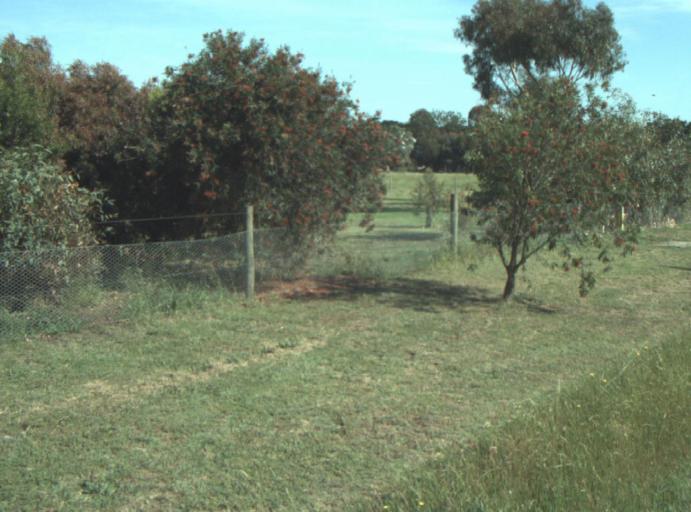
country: AU
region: Victoria
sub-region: Greater Geelong
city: Clifton Springs
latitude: -38.1697
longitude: 144.5151
